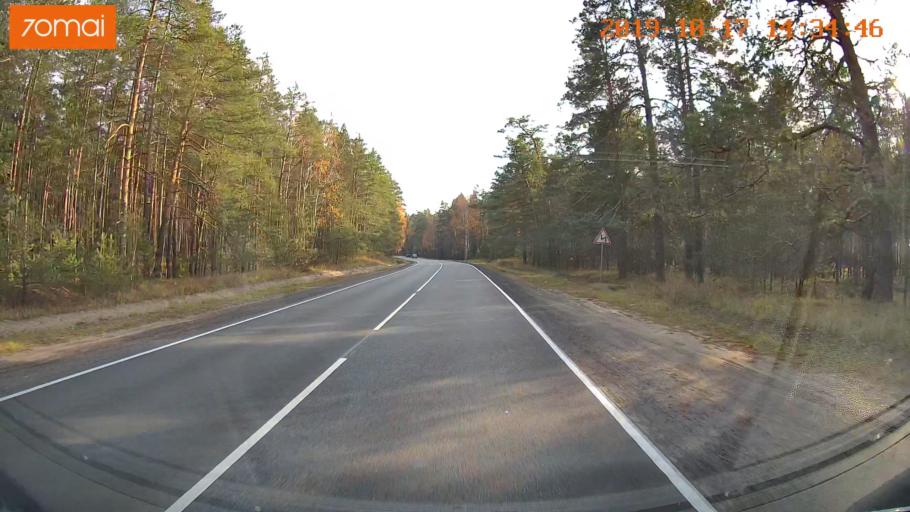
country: RU
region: Rjazan
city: Solotcha
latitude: 54.9077
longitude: 39.9992
